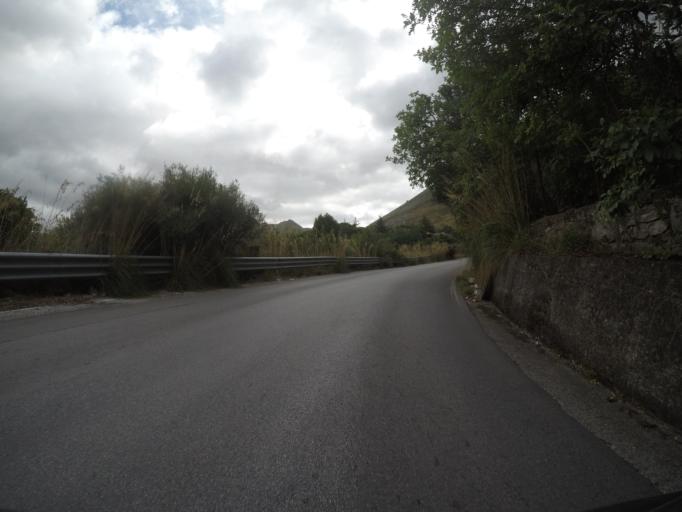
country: IT
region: Sicily
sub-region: Palermo
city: Montelepre
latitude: 38.1206
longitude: 13.1860
